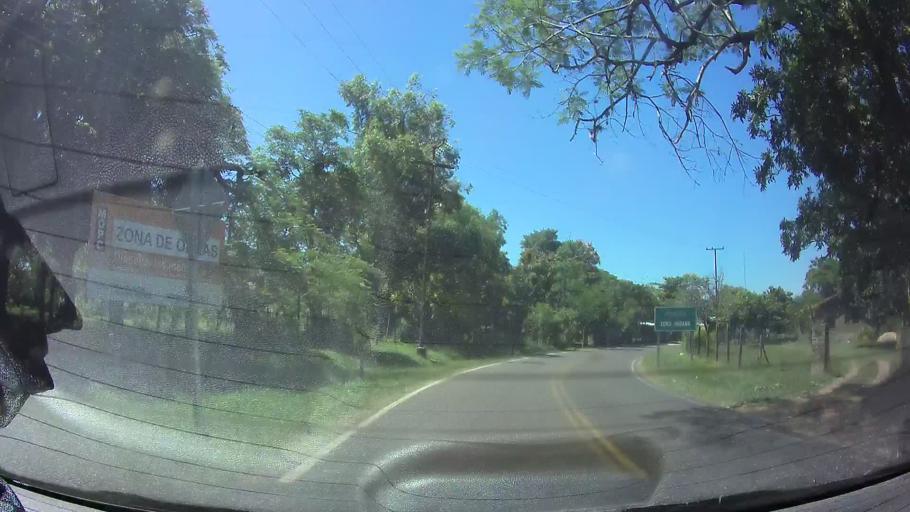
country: PY
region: Central
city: Aregua
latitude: -25.2691
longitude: -57.4129
